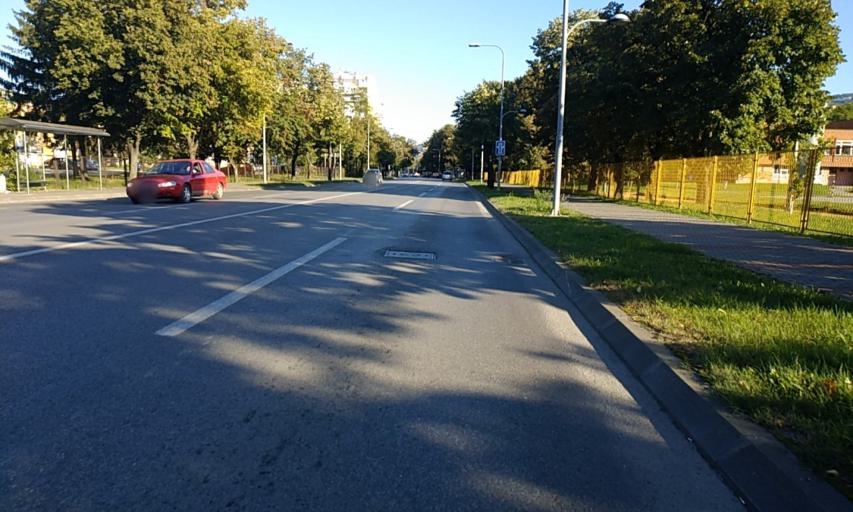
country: BA
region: Republika Srpska
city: Banja Luka
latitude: 44.7709
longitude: 17.1828
